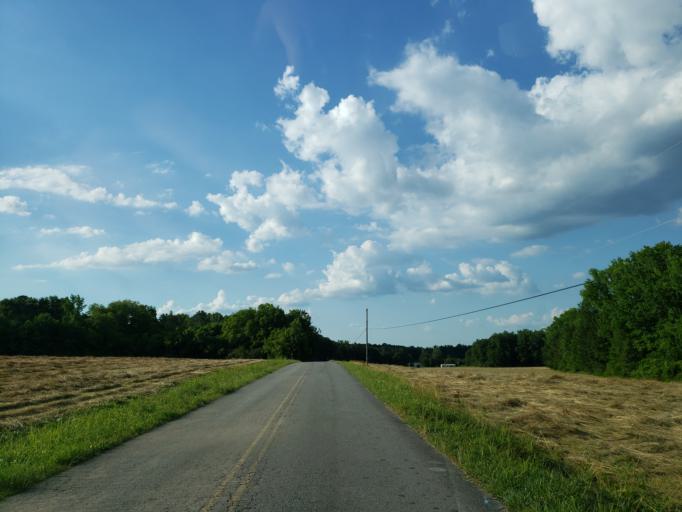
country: US
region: Georgia
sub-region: Haralson County
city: Buchanan
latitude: 33.9079
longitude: -85.2743
